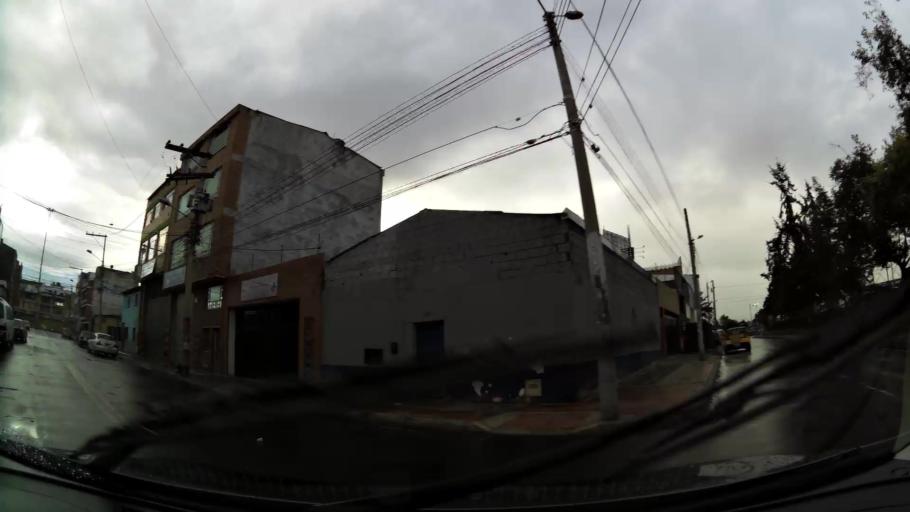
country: CO
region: Bogota D.C.
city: Barrio San Luis
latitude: 4.6777
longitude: -74.0847
